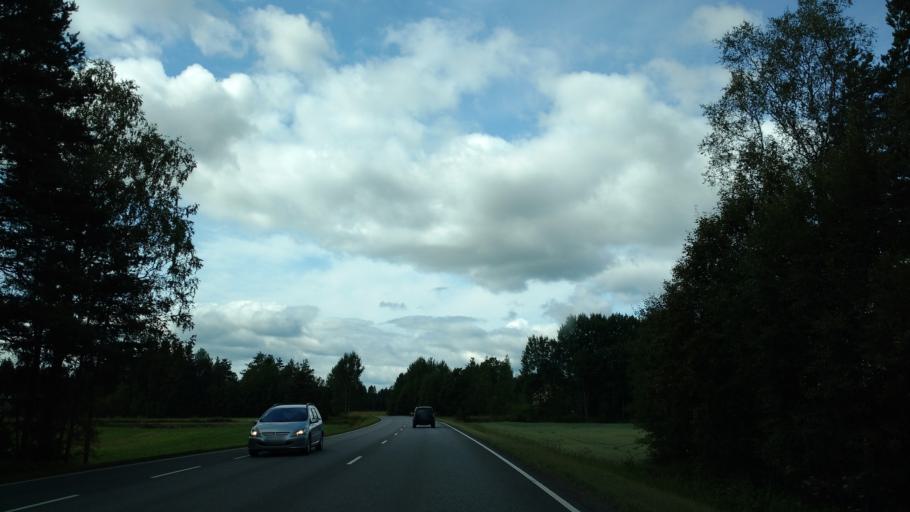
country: FI
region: Varsinais-Suomi
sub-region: Salo
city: Pernioe
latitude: 60.1779
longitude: 23.0418
